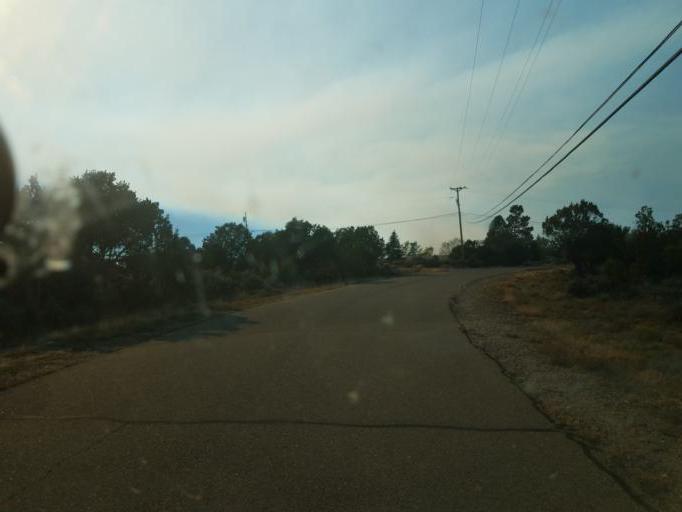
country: US
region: New Mexico
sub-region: Los Alamos County
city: White Rock
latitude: 35.8038
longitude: -106.2169
